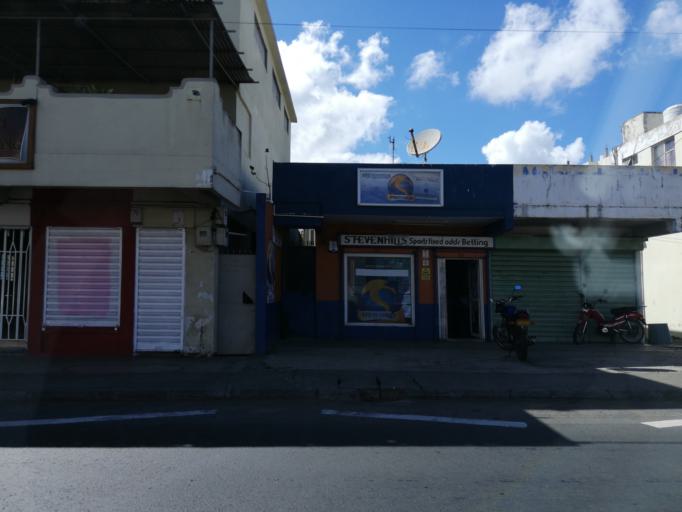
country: MU
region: Moka
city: Moka
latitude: -20.2158
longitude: 57.4694
